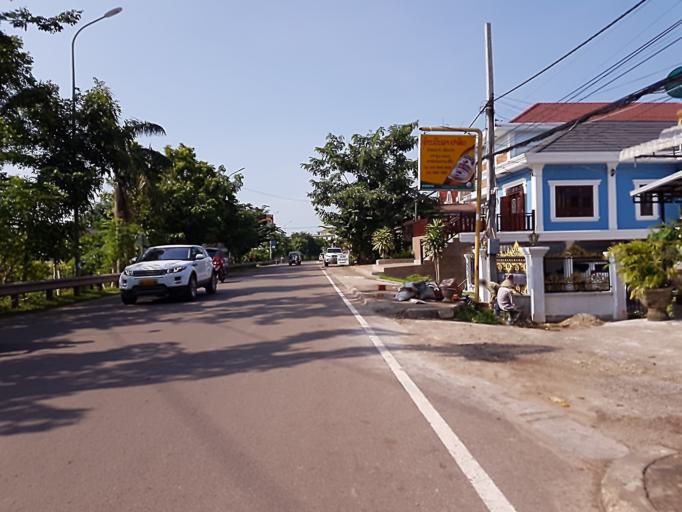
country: LA
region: Vientiane
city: Vientiane
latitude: 17.9479
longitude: 102.6227
